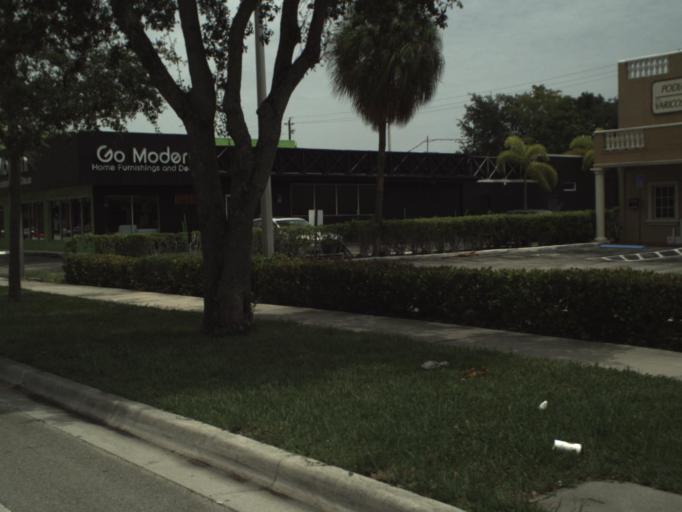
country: US
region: Florida
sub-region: Broward County
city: Oakland Park
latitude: 26.1792
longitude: -80.1195
